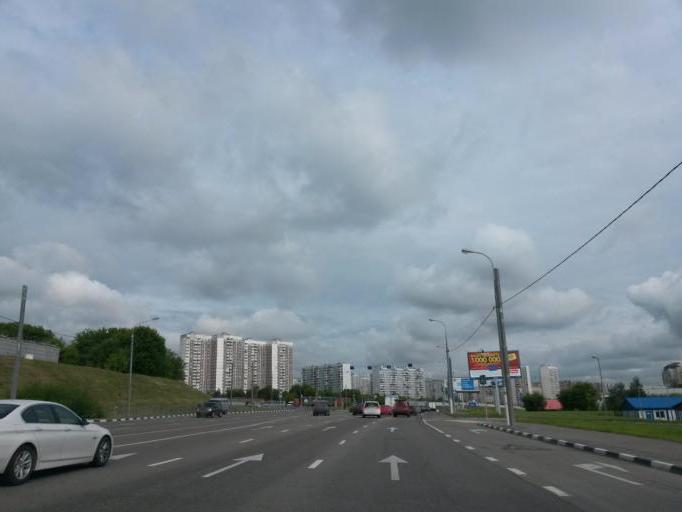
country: RU
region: Moscow
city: Zyablikovo
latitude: 55.6251
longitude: 37.7567
